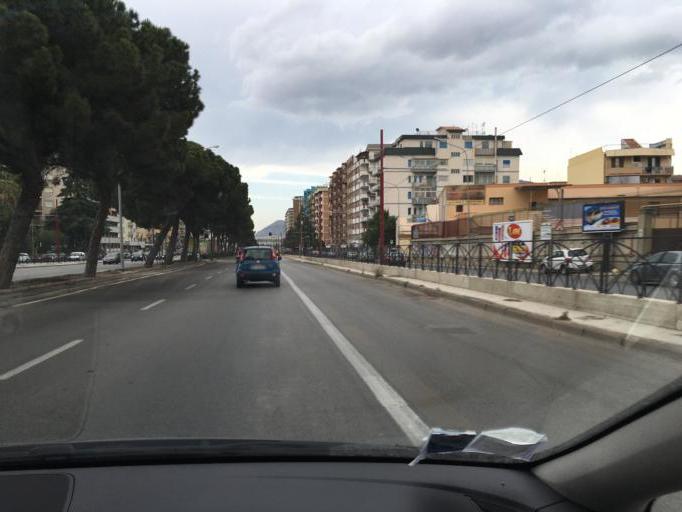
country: IT
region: Sicily
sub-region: Palermo
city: Palermo
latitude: 38.1216
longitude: 13.3290
